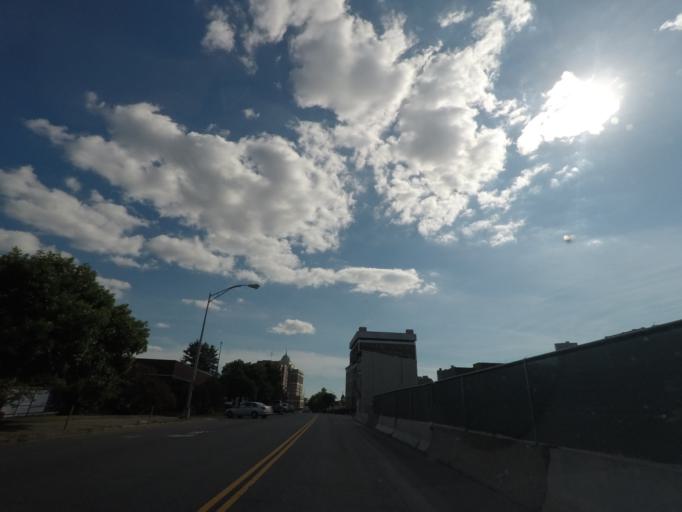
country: US
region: New York
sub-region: Albany County
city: Albany
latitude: 42.6572
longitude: -73.7484
